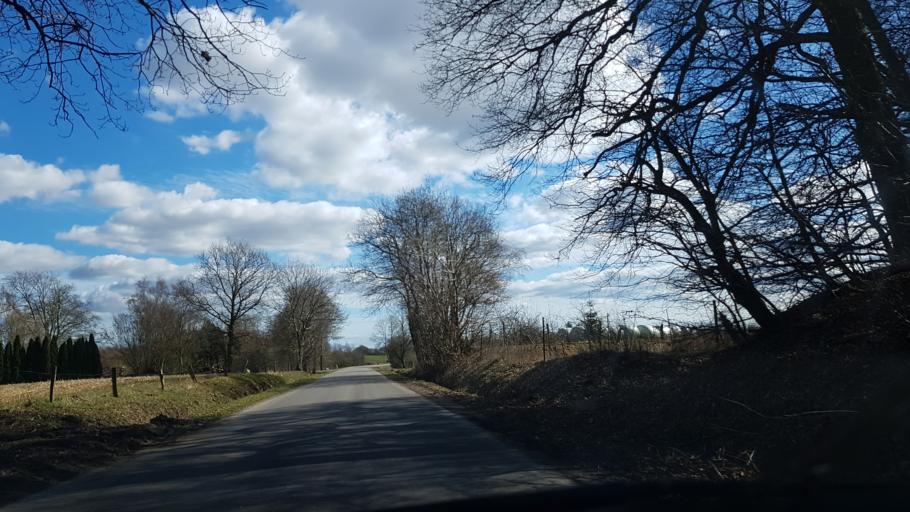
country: DK
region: South Denmark
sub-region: Kolding Kommune
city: Vamdrup
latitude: 55.3962
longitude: 9.2850
